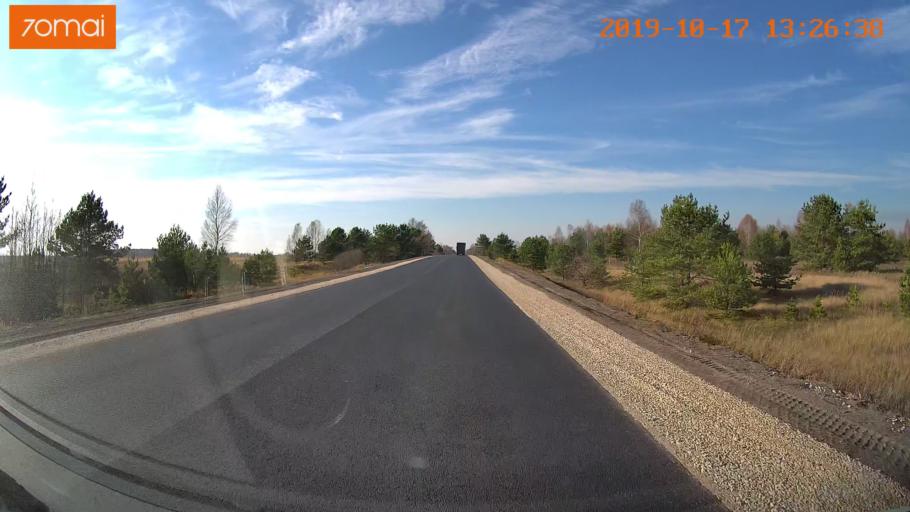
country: RU
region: Rjazan
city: Gus'-Zheleznyy
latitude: 55.1109
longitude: 40.9158
